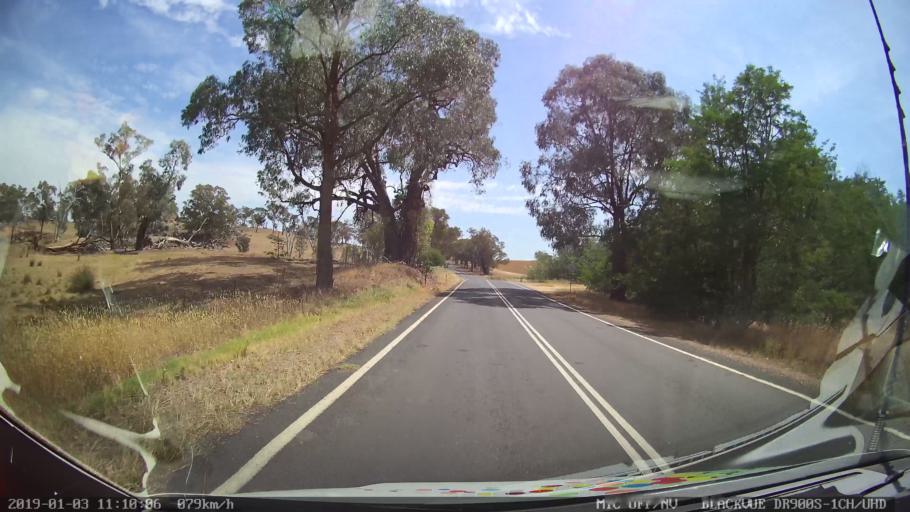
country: AU
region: New South Wales
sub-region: Young
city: Young
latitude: -34.2306
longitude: 148.2572
